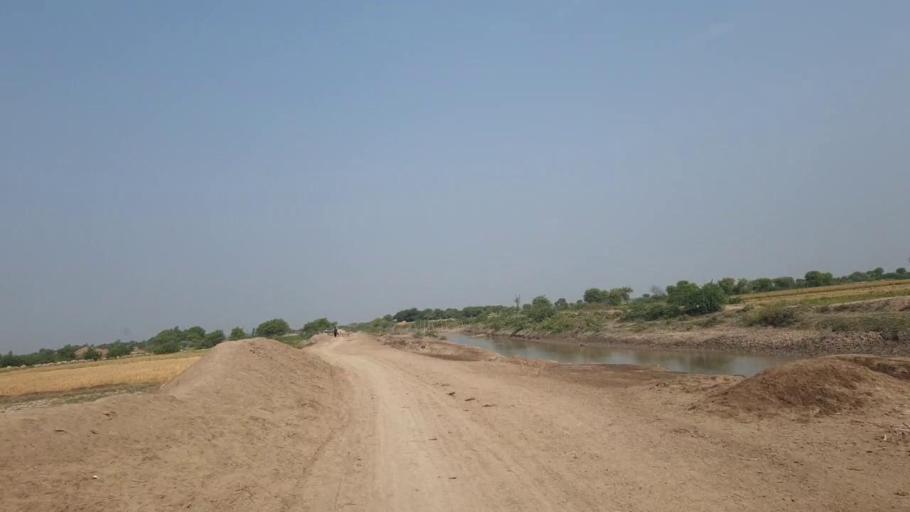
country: PK
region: Sindh
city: Badin
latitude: 24.7313
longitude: 68.7674
